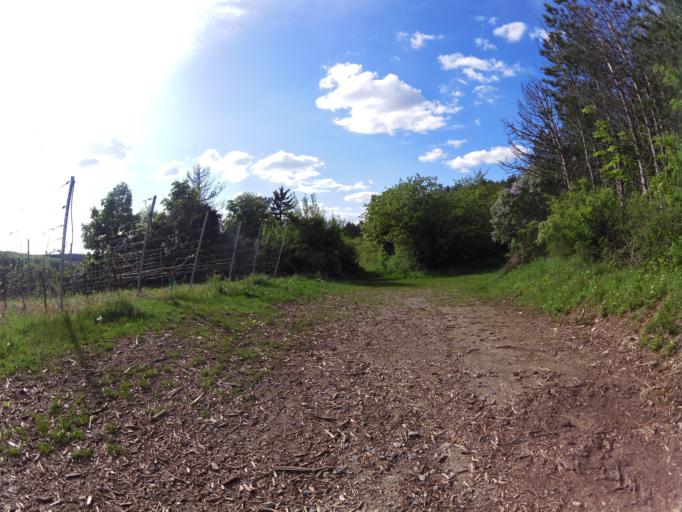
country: DE
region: Bavaria
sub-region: Regierungsbezirk Unterfranken
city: Erlabrunn
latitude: 49.8553
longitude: 9.8301
